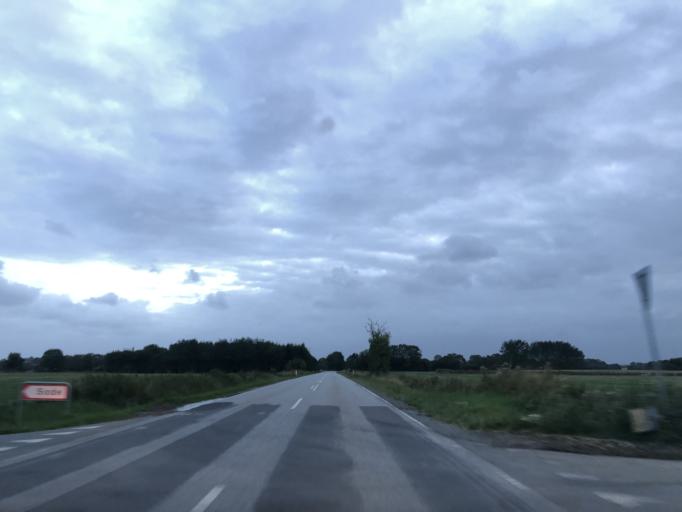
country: DK
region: South Denmark
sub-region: Haderslev Kommune
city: Starup
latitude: 55.2247
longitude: 9.6270
